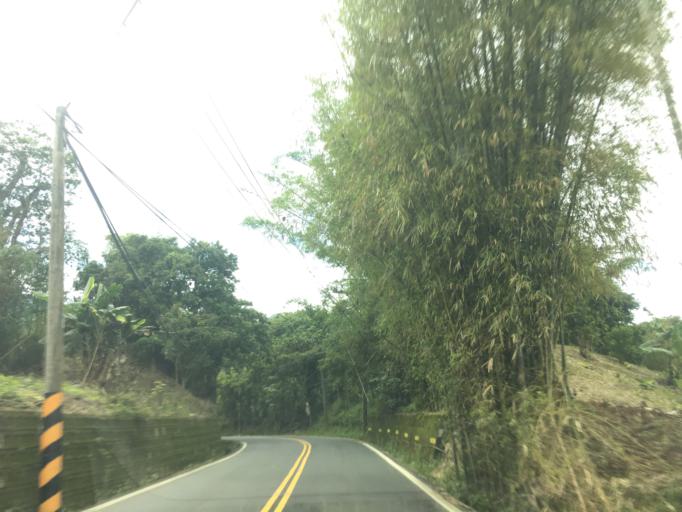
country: TW
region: Taiwan
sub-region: Yunlin
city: Douliu
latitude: 23.5709
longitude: 120.5660
